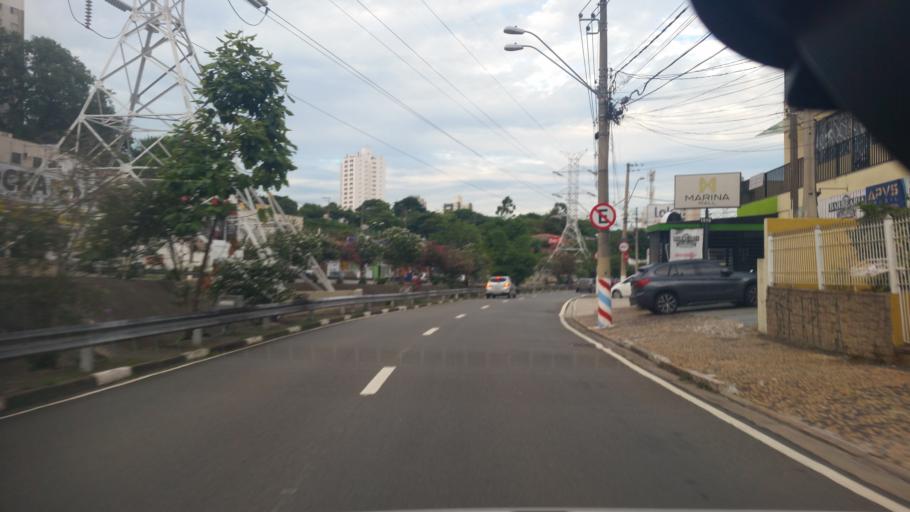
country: BR
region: Sao Paulo
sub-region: Campinas
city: Campinas
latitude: -22.8890
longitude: -47.0569
